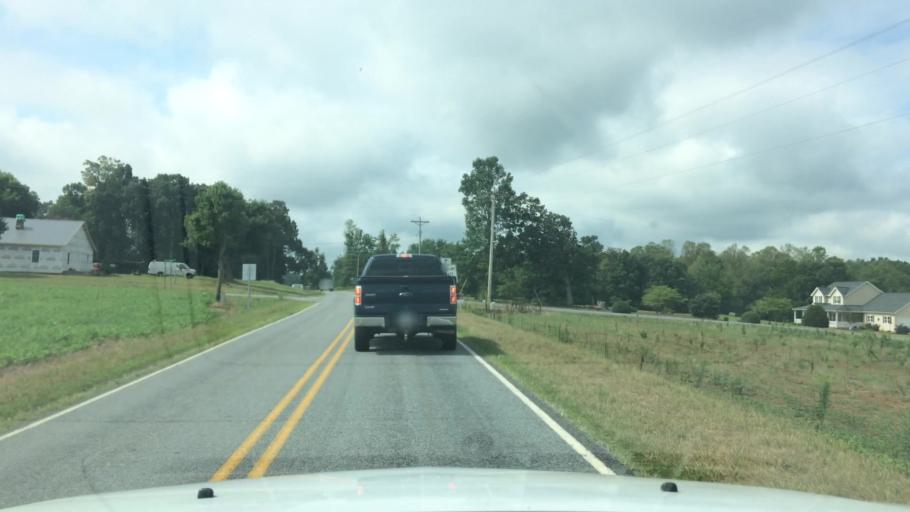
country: US
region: North Carolina
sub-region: Yadkin County
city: Jonesville
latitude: 36.1004
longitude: -80.8623
